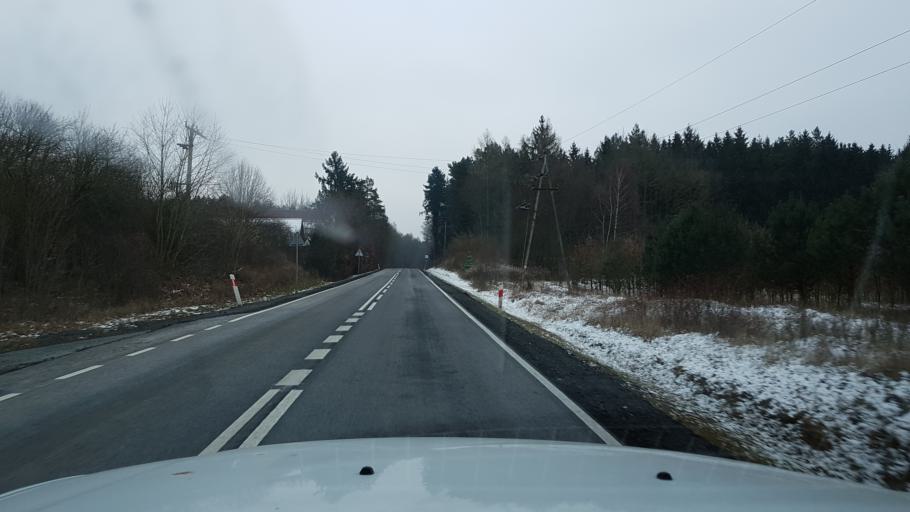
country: PL
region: West Pomeranian Voivodeship
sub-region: Powiat gryfinski
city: Widuchowa
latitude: 53.1129
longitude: 14.4043
